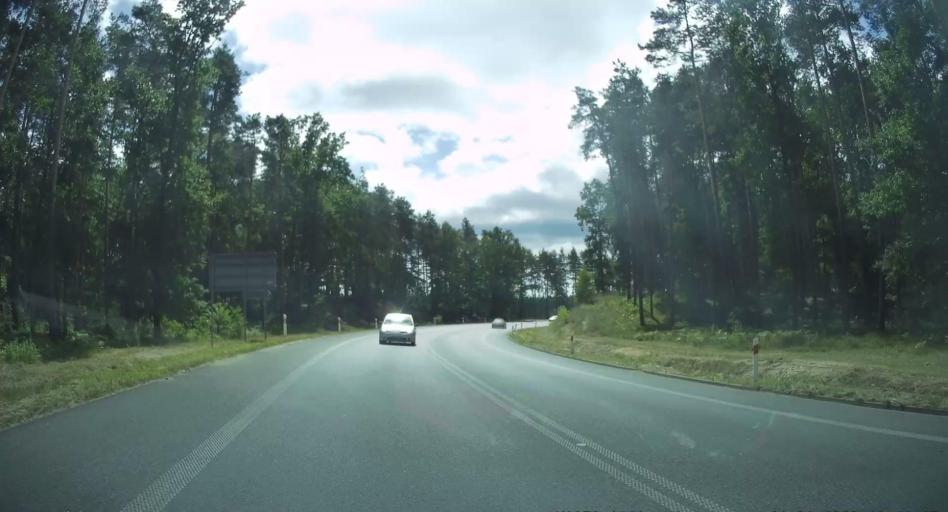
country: PL
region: Subcarpathian Voivodeship
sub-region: Powiat mielecki
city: Mielec
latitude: 50.3140
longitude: 21.5035
